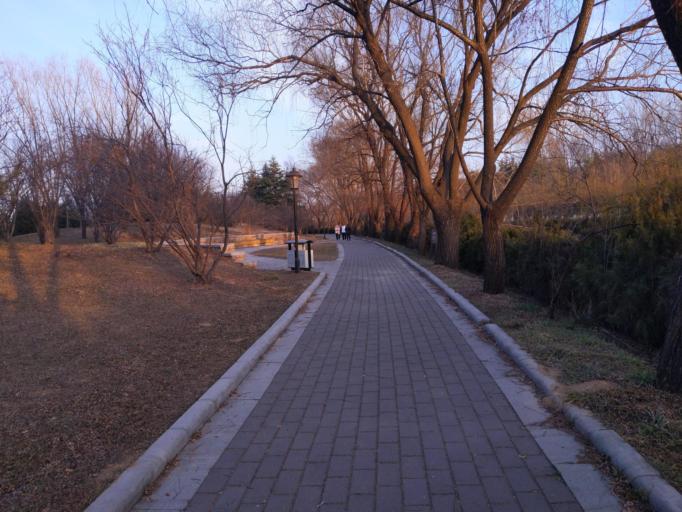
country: CN
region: Henan Sheng
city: Puyang
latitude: 35.7814
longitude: 114.9474
